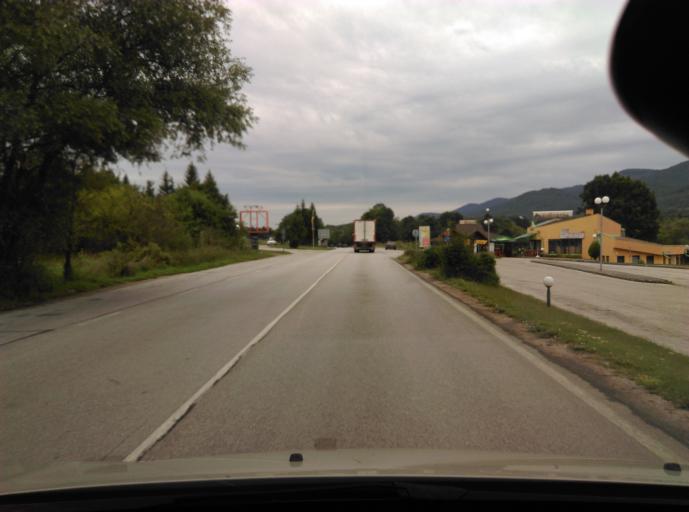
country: BG
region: Lovech
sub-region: Obshtina Ugurchin
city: Ugurchin
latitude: 43.0403
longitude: 24.5297
